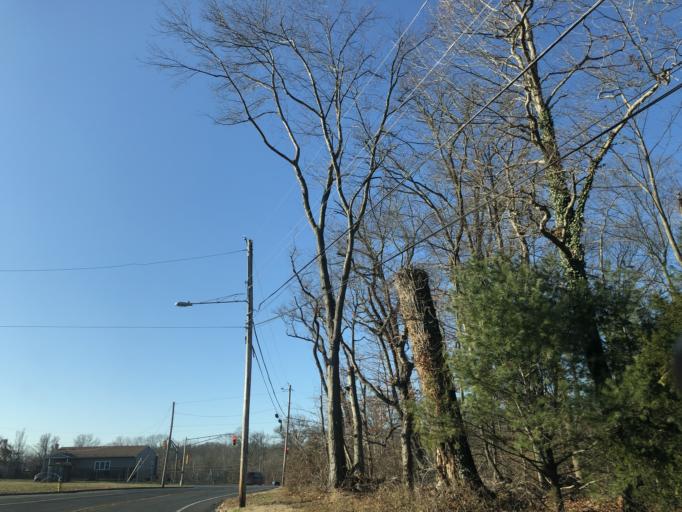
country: US
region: New Jersey
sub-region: Gloucester County
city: Wenonah
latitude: 39.7980
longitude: -75.1167
